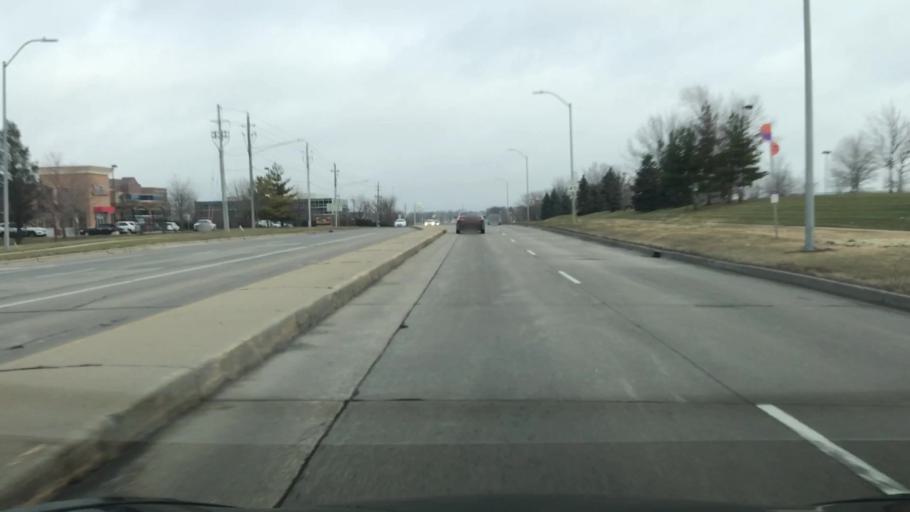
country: US
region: Iowa
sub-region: Polk County
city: Clive
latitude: 41.6005
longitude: -93.7900
